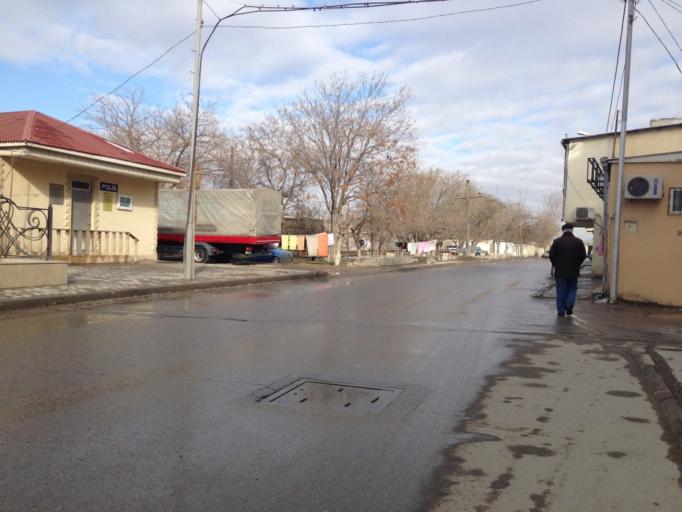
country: AZ
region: Baki
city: Baku
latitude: 40.3960
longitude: 49.8908
